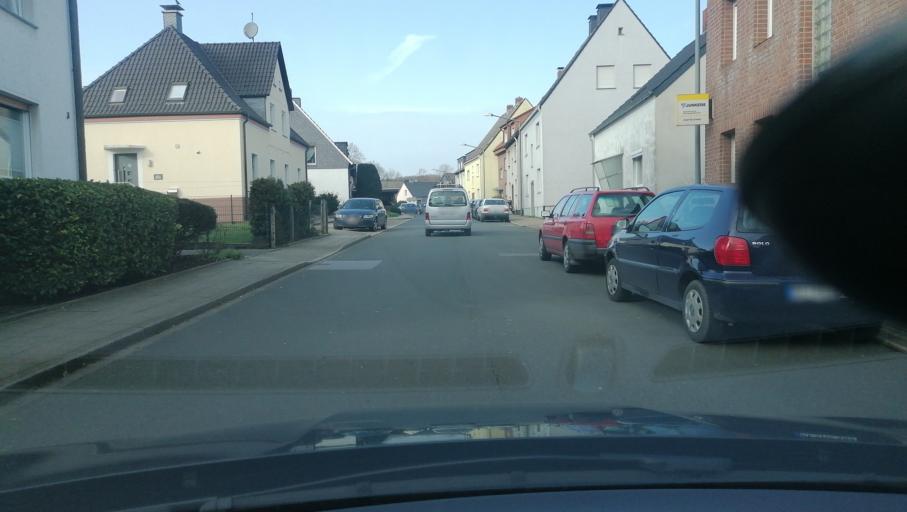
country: DE
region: North Rhine-Westphalia
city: Herten
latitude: 51.6046
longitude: 7.1594
